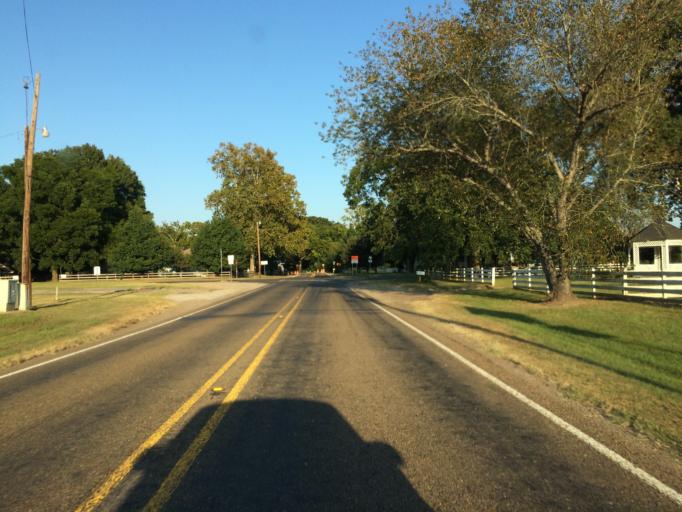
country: US
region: Texas
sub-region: Wood County
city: Quitman
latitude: 32.7173
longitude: -95.3671
